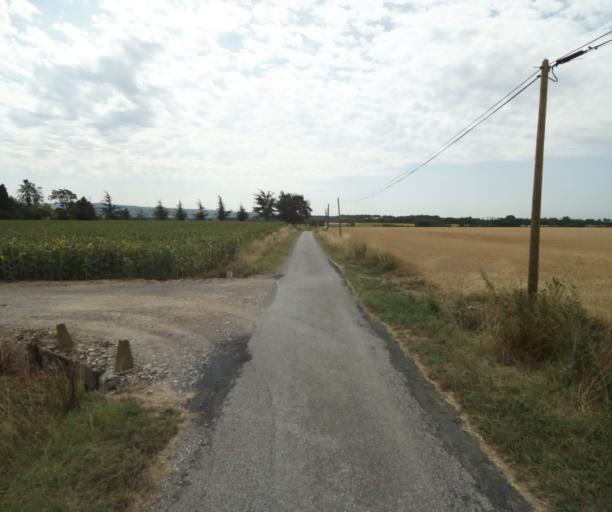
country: FR
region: Midi-Pyrenees
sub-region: Departement de la Haute-Garonne
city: Saint-Felix-Lauragais
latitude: 43.4409
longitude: 1.9103
